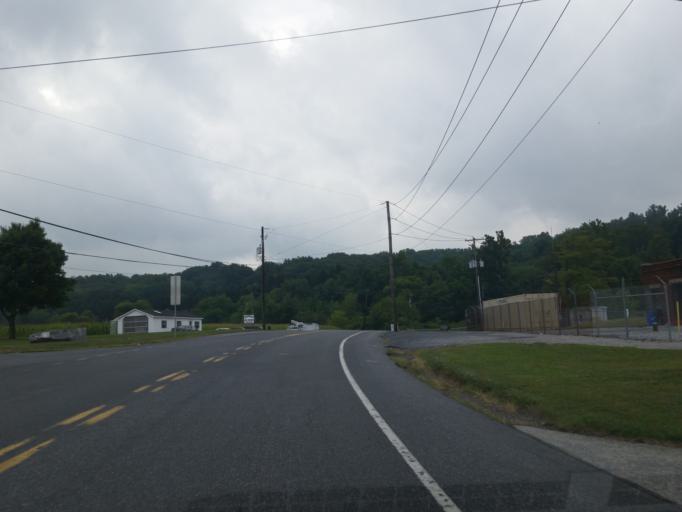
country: US
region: Pennsylvania
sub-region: Lancaster County
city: Brickerville
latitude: 40.2770
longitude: -76.2963
